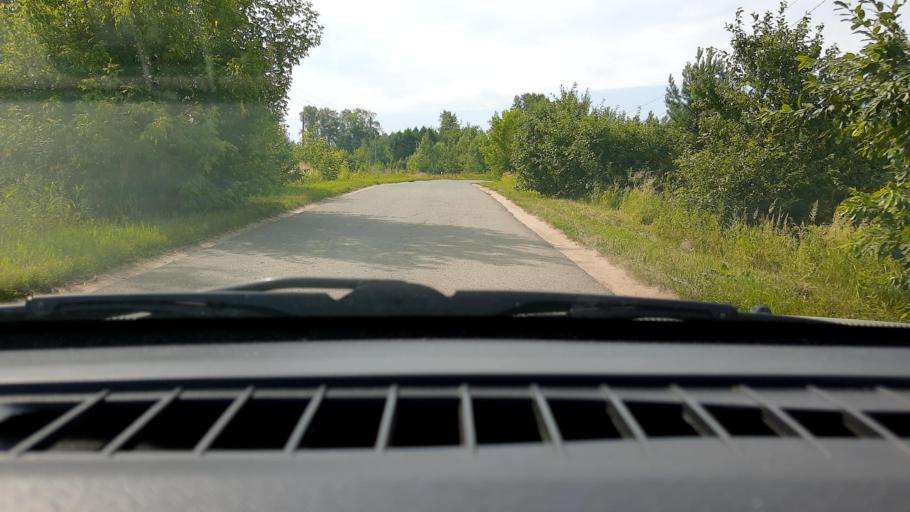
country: RU
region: Nizjnij Novgorod
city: Lukino
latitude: 56.4167
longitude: 43.7128
